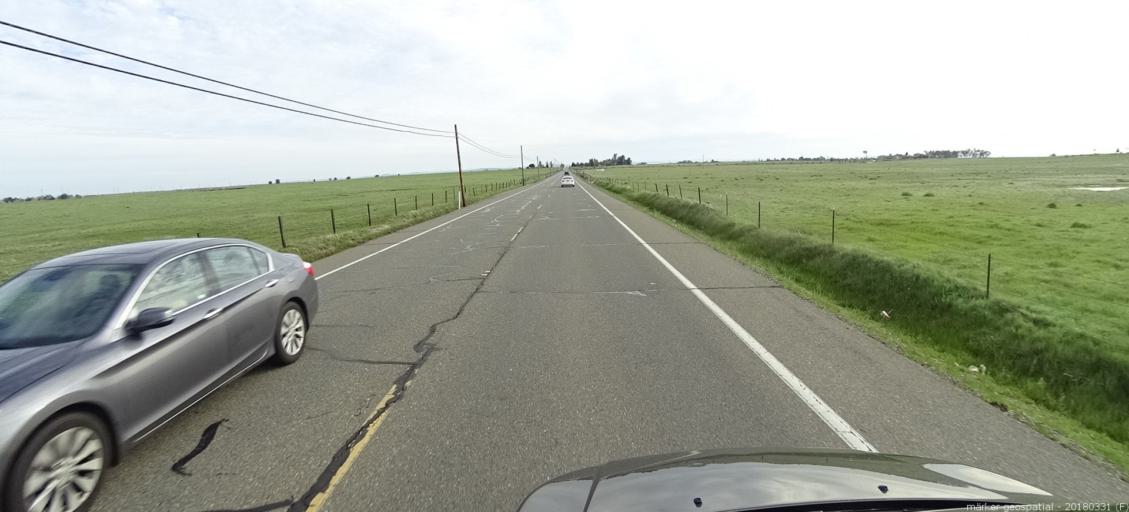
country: US
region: California
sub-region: Sacramento County
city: Wilton
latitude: 38.4880
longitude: -121.2389
